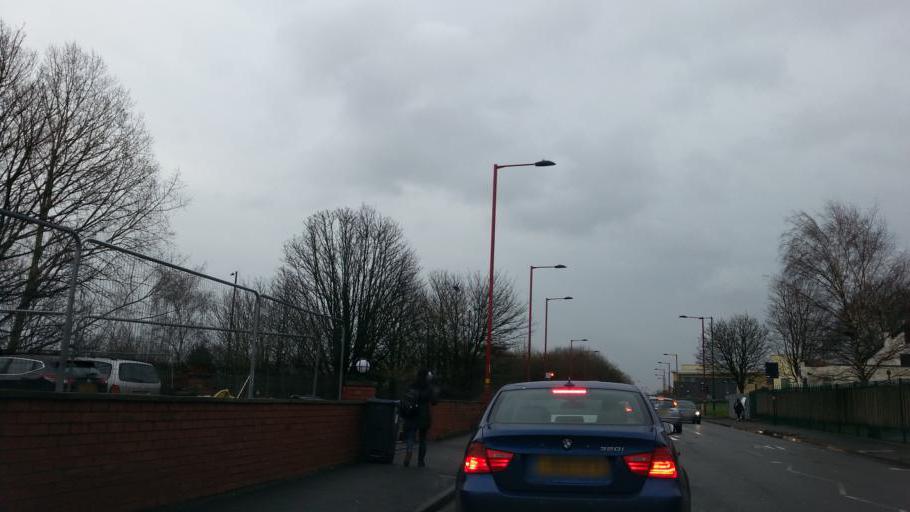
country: GB
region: England
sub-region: City and Borough of Birmingham
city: Hockley
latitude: 52.4890
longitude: -1.9391
